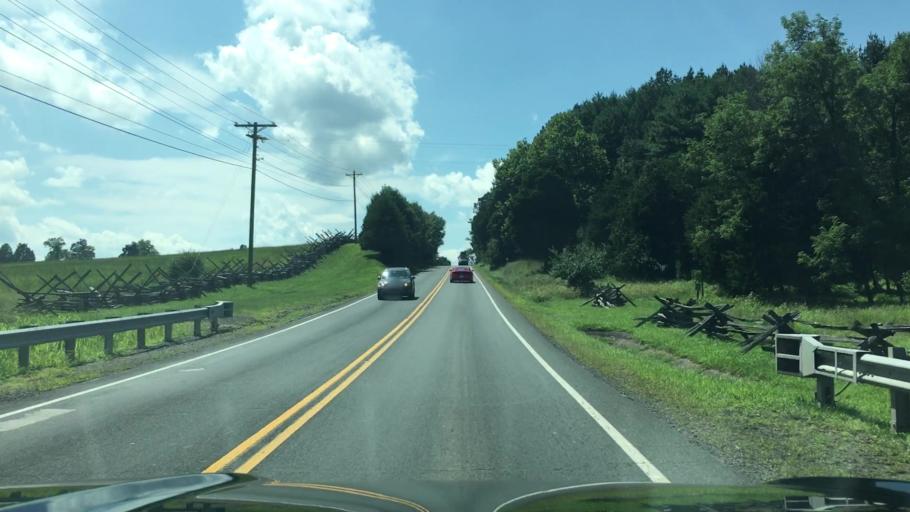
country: US
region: Virginia
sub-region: Prince William County
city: Sudley
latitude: 38.8215
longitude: -77.5151
